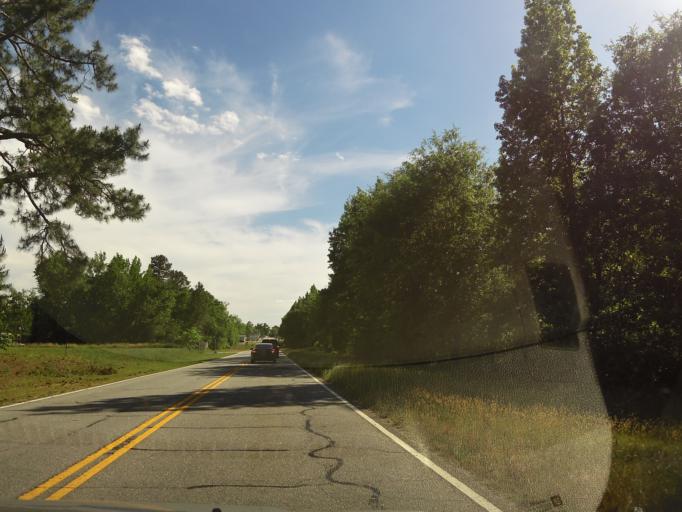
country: US
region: South Carolina
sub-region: Bamberg County
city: Denmark
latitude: 33.1855
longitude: -81.1834
